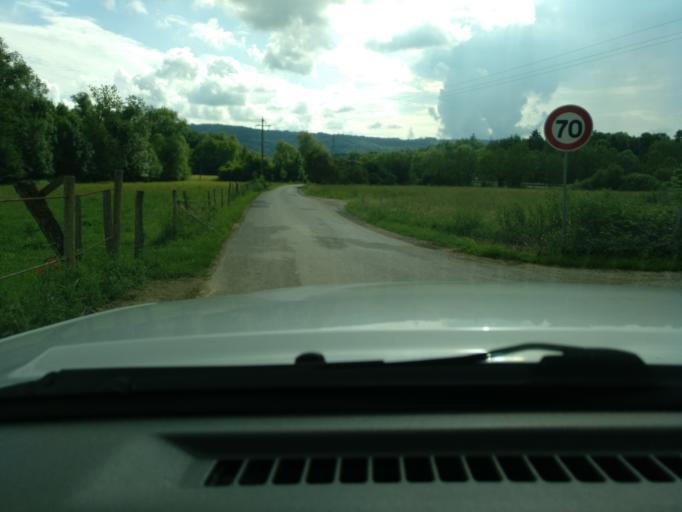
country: FR
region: Rhone-Alpes
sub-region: Departement de la Haute-Savoie
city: Cornier
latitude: 46.1047
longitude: 6.3090
